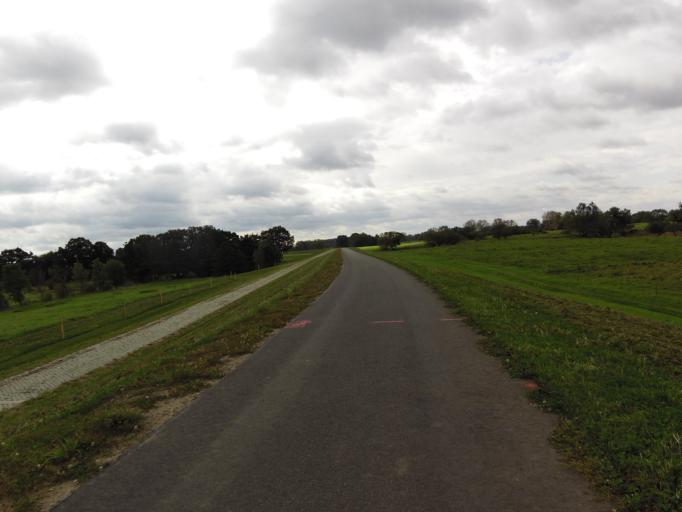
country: DE
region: Saxony-Anhalt
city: Havelberg
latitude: 52.8585
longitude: 12.0349
